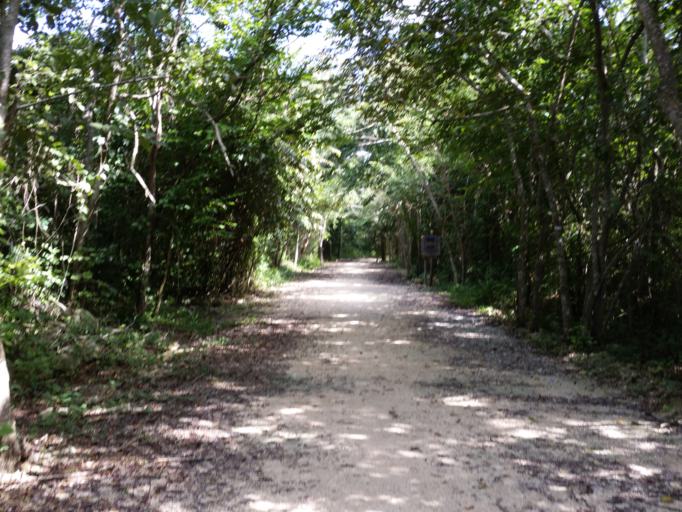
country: MX
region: Yucatan
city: Temozon
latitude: 20.8886
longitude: -88.1258
